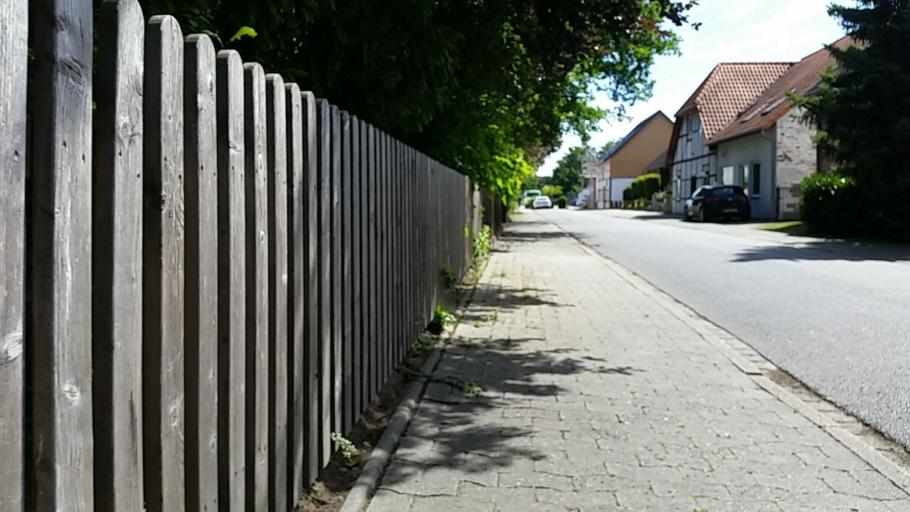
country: DE
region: Lower Saxony
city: Wolfsburg
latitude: 52.4450
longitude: 10.7815
